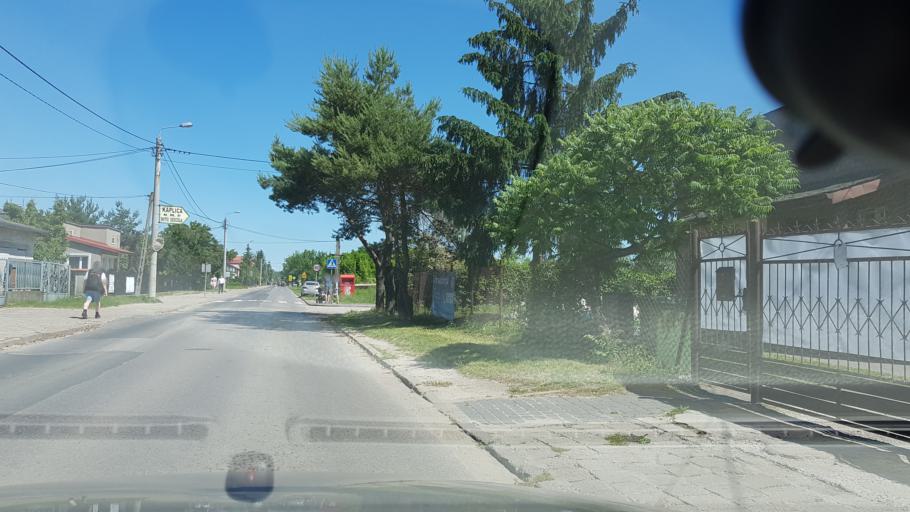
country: PL
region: Masovian Voivodeship
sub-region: Powiat wolominski
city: Marki
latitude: 52.3150
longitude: 21.1125
